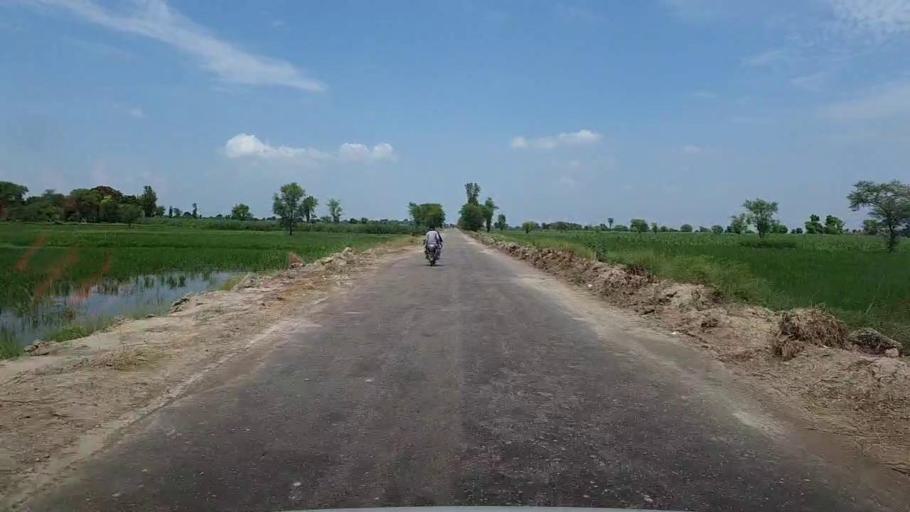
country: PK
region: Sindh
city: Bhiria
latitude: 26.9260
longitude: 68.2097
